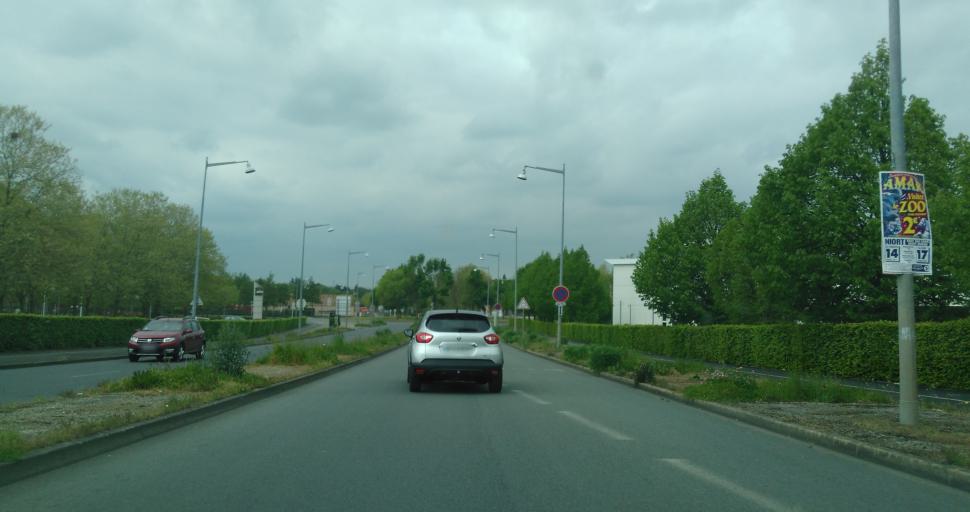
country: FR
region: Poitou-Charentes
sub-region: Departement des Deux-Sevres
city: Niort
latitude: 46.3319
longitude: -0.4837
